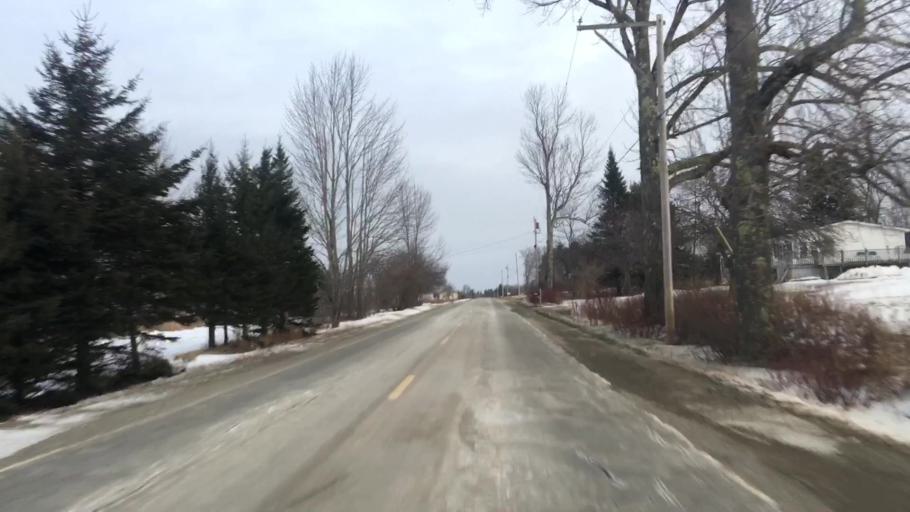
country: US
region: Maine
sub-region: Hancock County
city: Franklin
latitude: 44.7152
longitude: -68.3371
